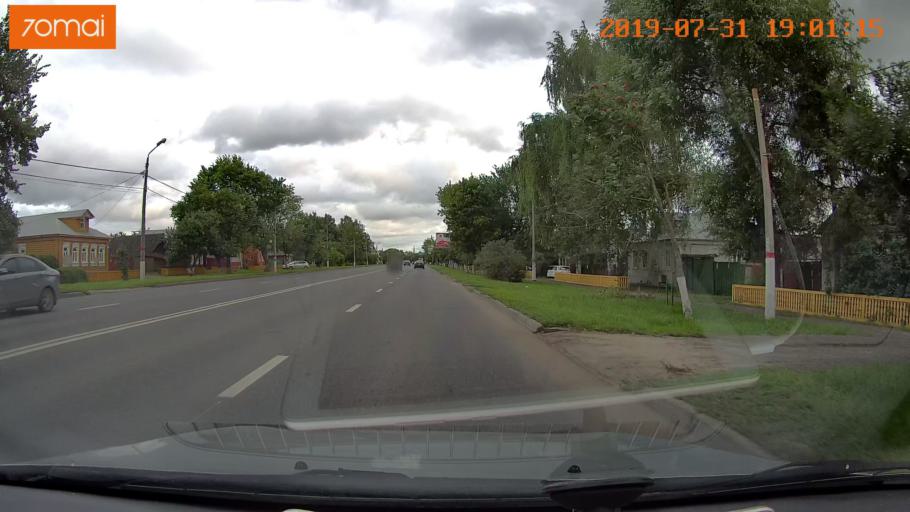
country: RU
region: Moskovskaya
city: Raduzhnyy
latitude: 55.1281
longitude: 38.7285
